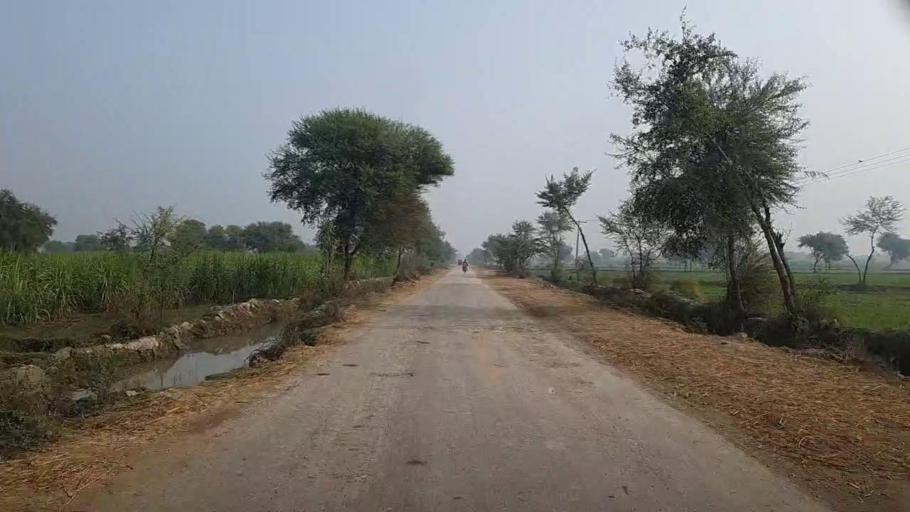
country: PK
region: Sindh
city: Dadu
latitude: 26.8334
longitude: 67.7701
